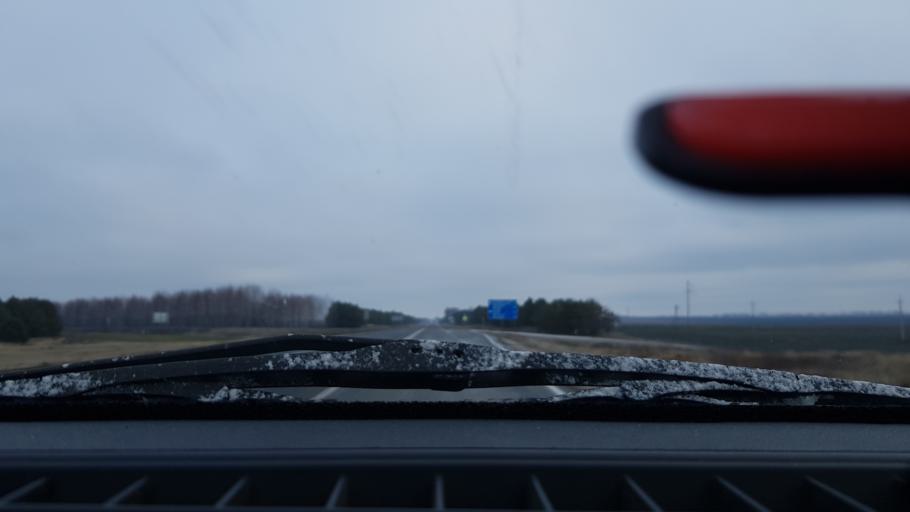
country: RU
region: Tatarstan
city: Kuybyshevskiy Zaton
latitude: 54.9633
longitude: 49.4972
